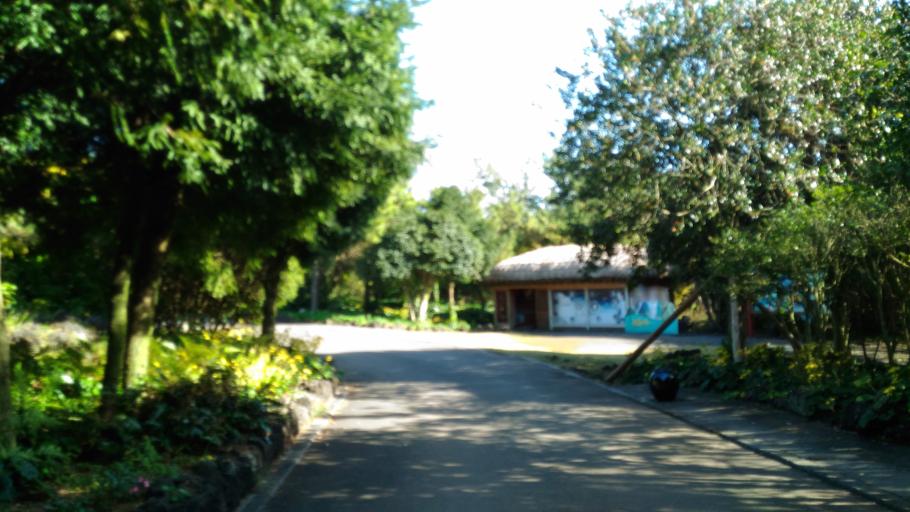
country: KR
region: Jeju-do
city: Seogwipo
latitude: 33.3207
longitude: 126.8430
